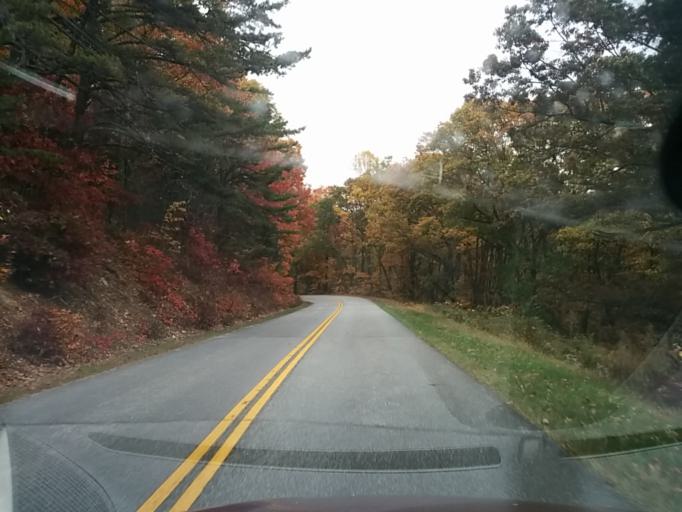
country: US
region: Virginia
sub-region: City of Buena Vista
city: Buena Vista
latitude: 37.7879
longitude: -79.2698
